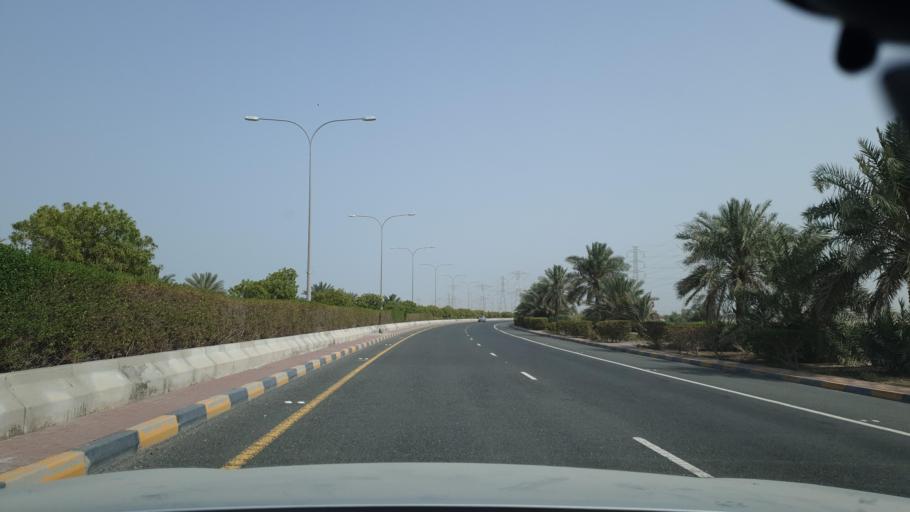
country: QA
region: Al Wakrah
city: Umm Sa'id
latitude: 25.0083
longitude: 51.5586
